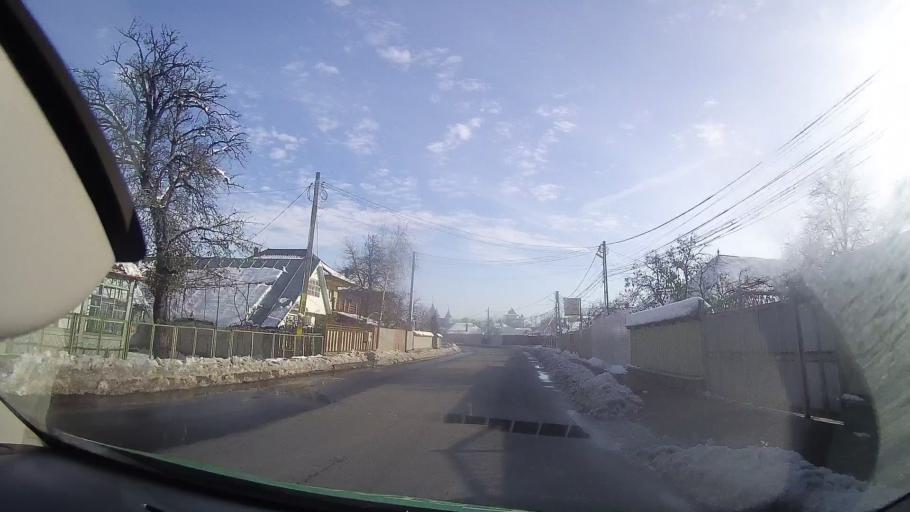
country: RO
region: Neamt
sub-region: Oras Targu Neamt
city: Humulesti
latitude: 47.1999
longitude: 26.3480
